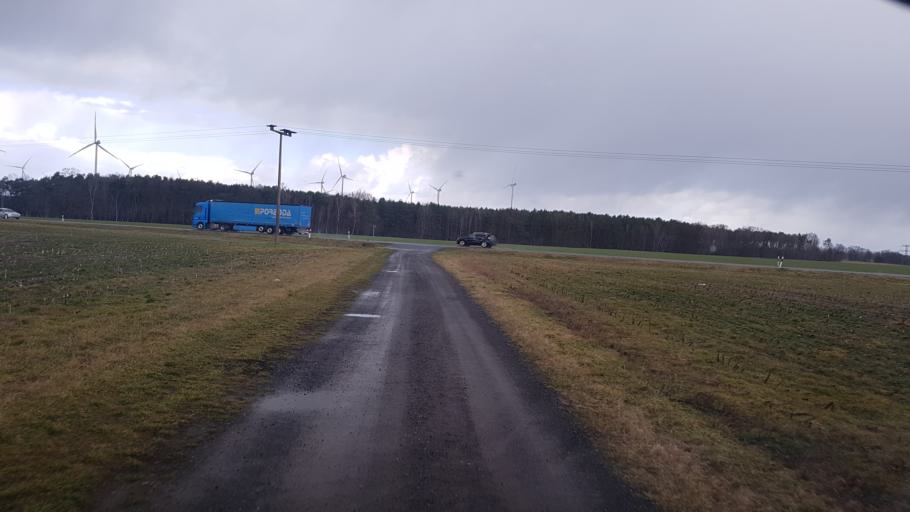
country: DE
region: Brandenburg
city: Sallgast
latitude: 51.6129
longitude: 13.8390
